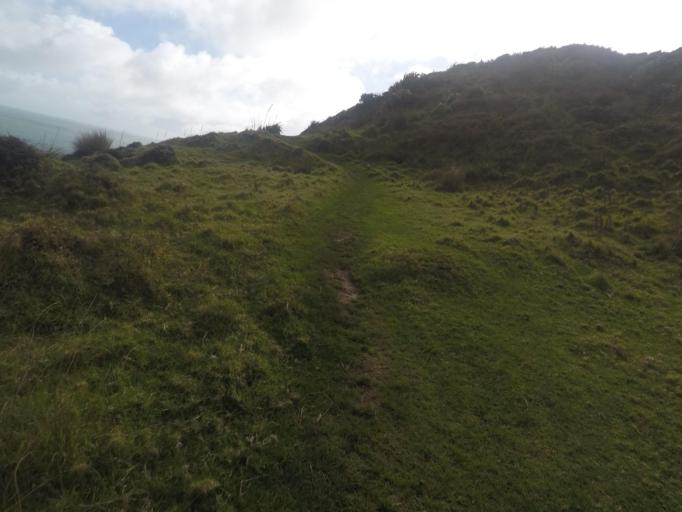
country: NZ
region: Auckland
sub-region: Auckland
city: Muriwai Beach
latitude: -36.8695
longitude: 174.4355
